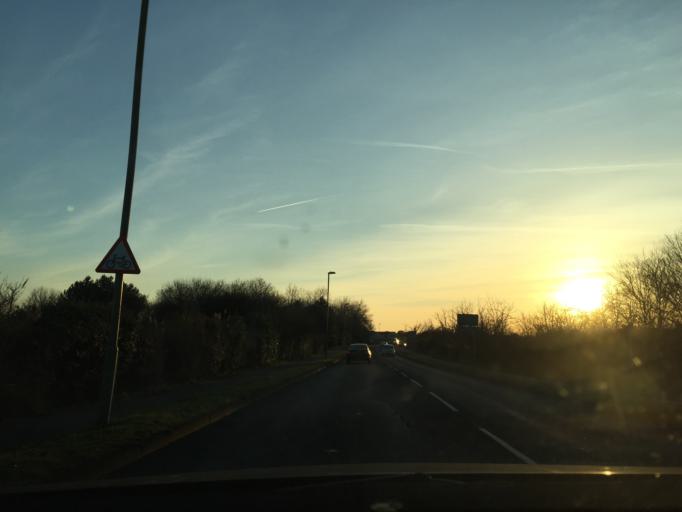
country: GB
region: England
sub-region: Hampshire
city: Lee-on-the-Solent
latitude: 50.7922
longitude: -1.1691
